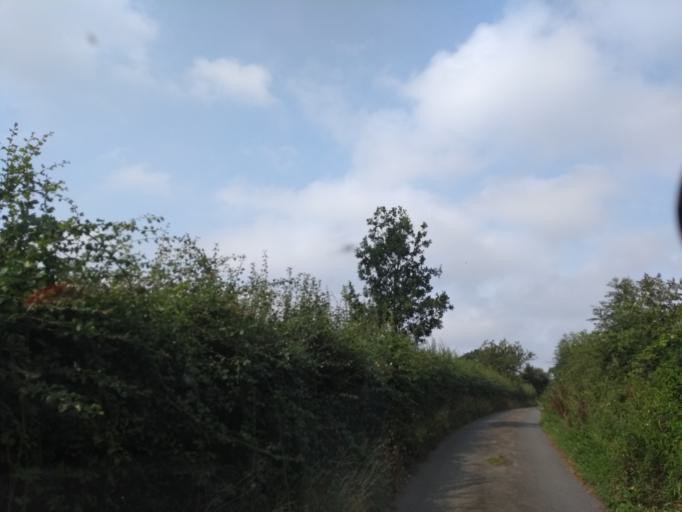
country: GB
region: England
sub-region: Somerset
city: Chard
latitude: 50.8767
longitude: -3.0616
